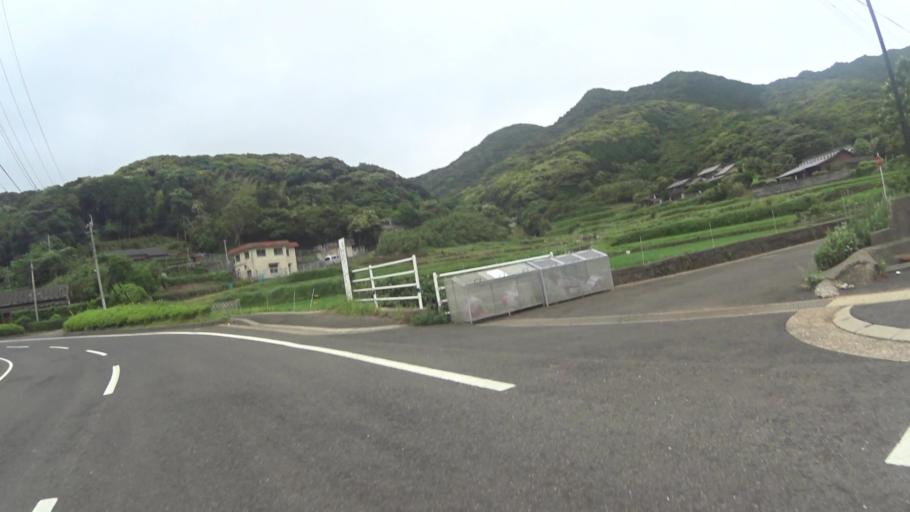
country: JP
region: Nagasaki
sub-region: Hirado Shi
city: Hirado
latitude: 33.1857
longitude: 129.3651
